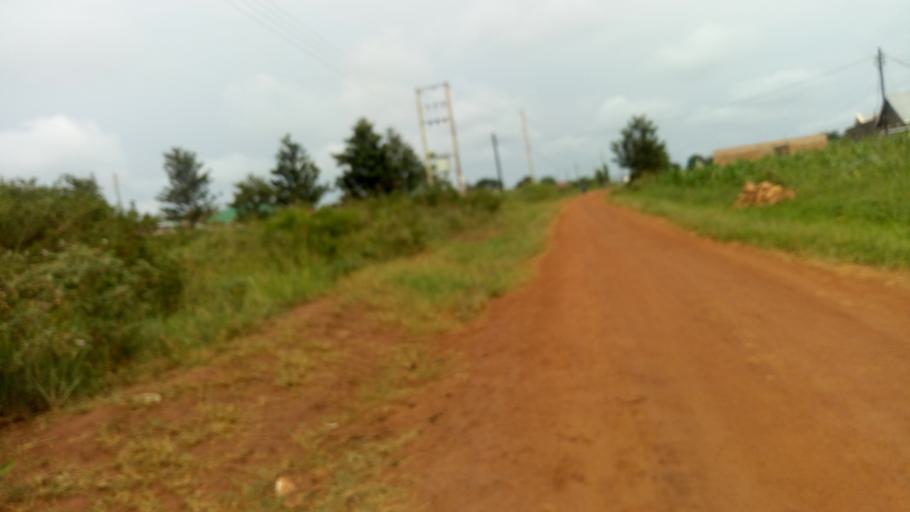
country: UG
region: Western Region
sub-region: Kiryandongo District
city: Kiryandongo
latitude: 1.8037
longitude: 32.0124
